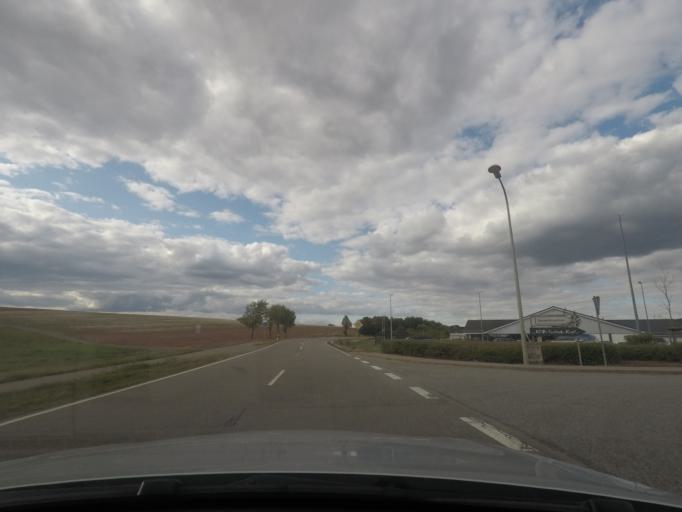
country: DE
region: Rheinland-Pfalz
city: Lohnsfeld
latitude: 49.5578
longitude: 7.8586
